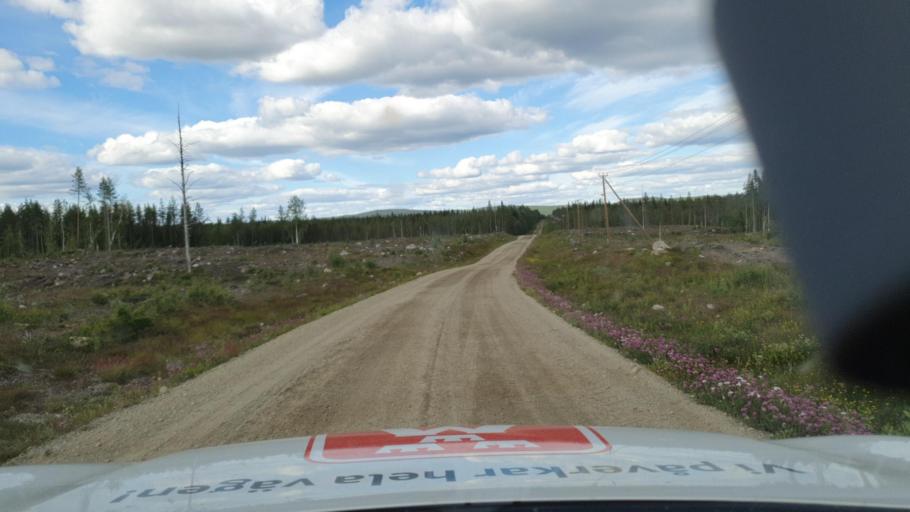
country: SE
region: Vaesterbotten
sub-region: Lycksele Kommun
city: Lycksele
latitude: 64.3047
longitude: 18.2878
